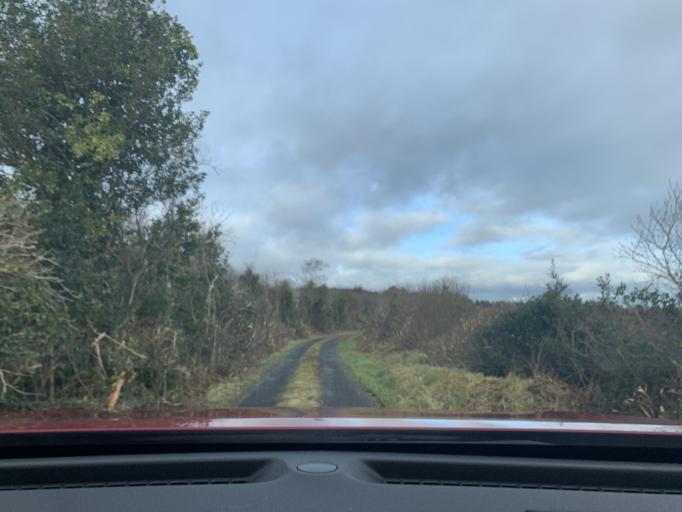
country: IE
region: Connaught
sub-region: Roscommon
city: Ballaghaderreen
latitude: 53.9297
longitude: -8.5582
